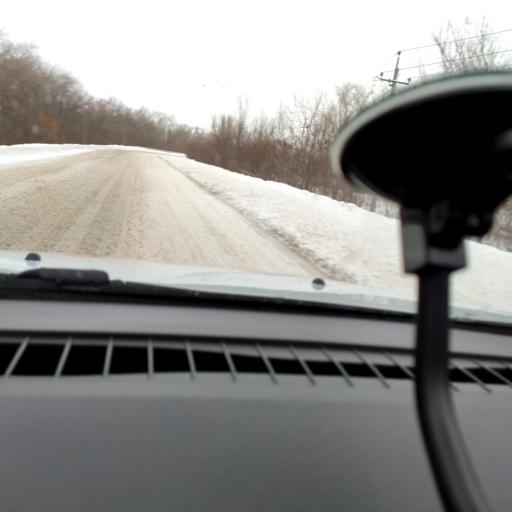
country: RU
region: Samara
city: Dubovyy Umet
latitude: 53.0381
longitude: 50.2319
